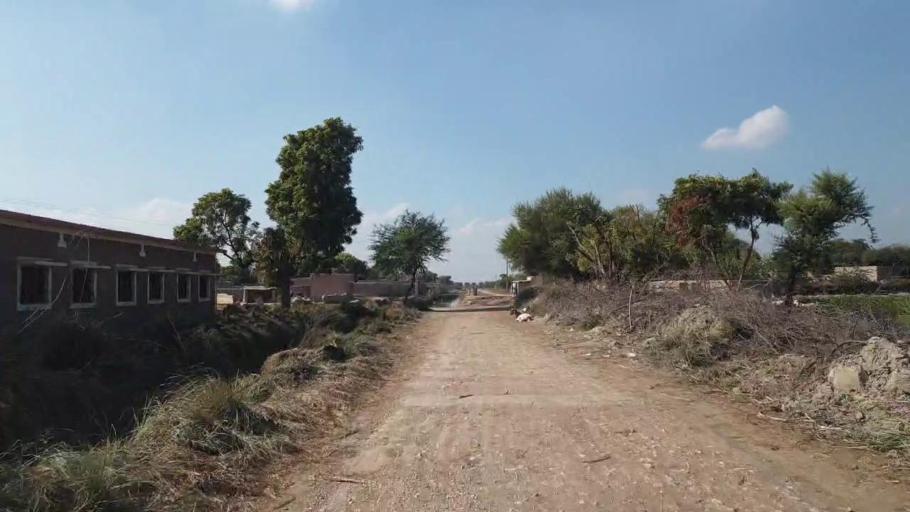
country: PK
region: Sindh
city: Shahpur Chakar
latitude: 26.0839
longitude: 68.5661
